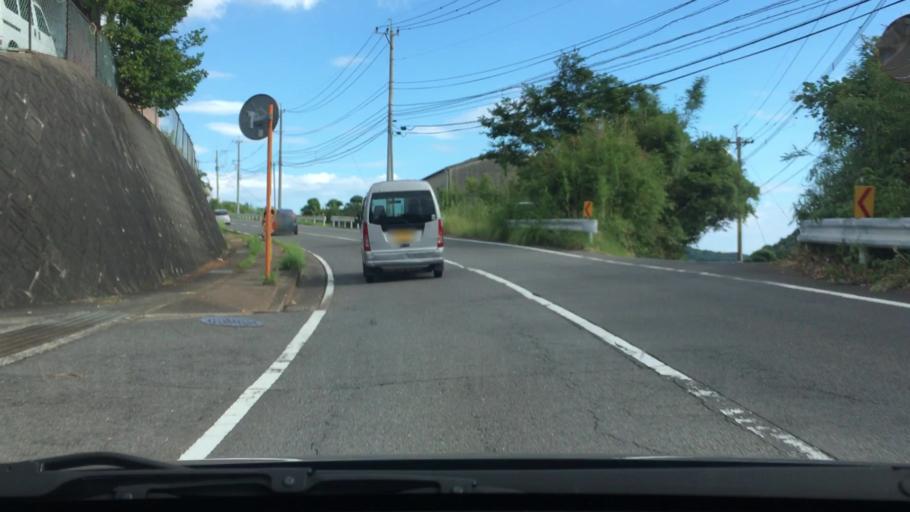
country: JP
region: Nagasaki
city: Togitsu
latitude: 32.8213
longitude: 129.7344
